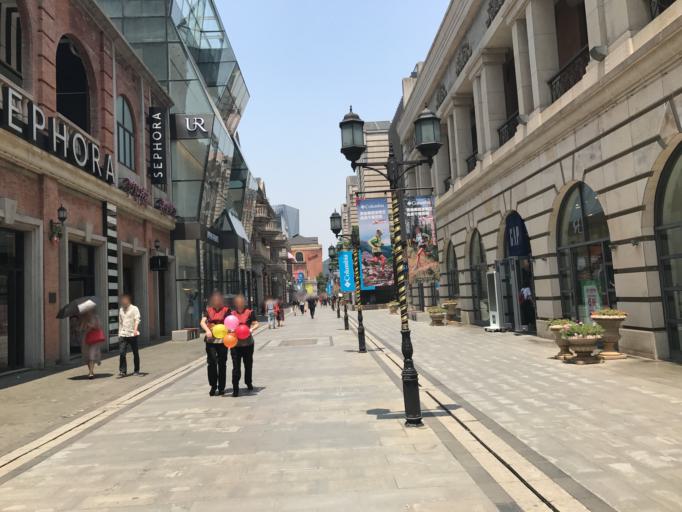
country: CN
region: Hubei
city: Jiang'an
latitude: 30.5592
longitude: 114.3355
